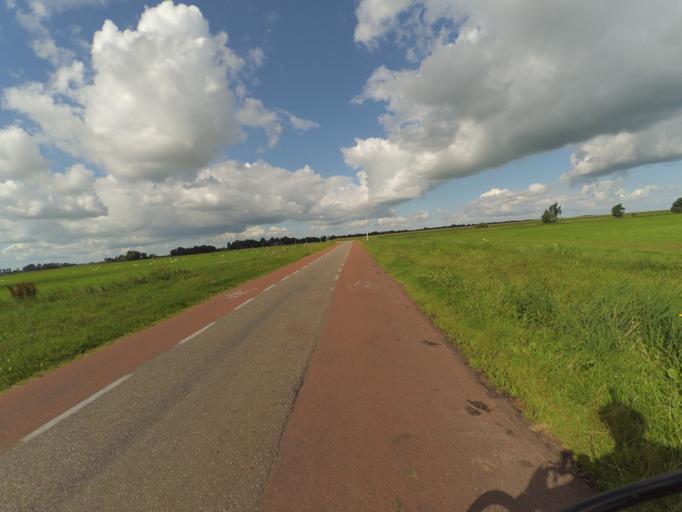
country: NL
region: Friesland
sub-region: Gemeente Dantumadiel
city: Rinsumageast
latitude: 53.2593
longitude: 5.9424
